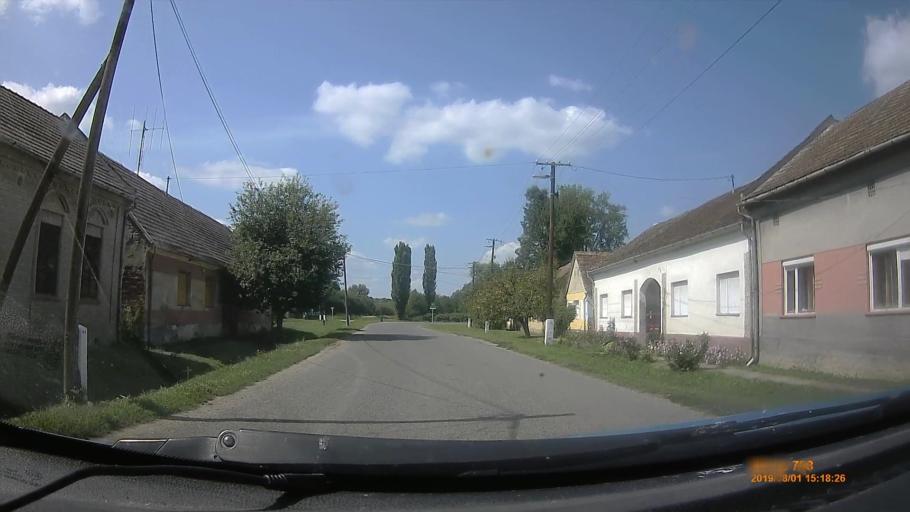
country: HU
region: Baranya
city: Sellye
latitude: 45.8484
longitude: 17.8162
